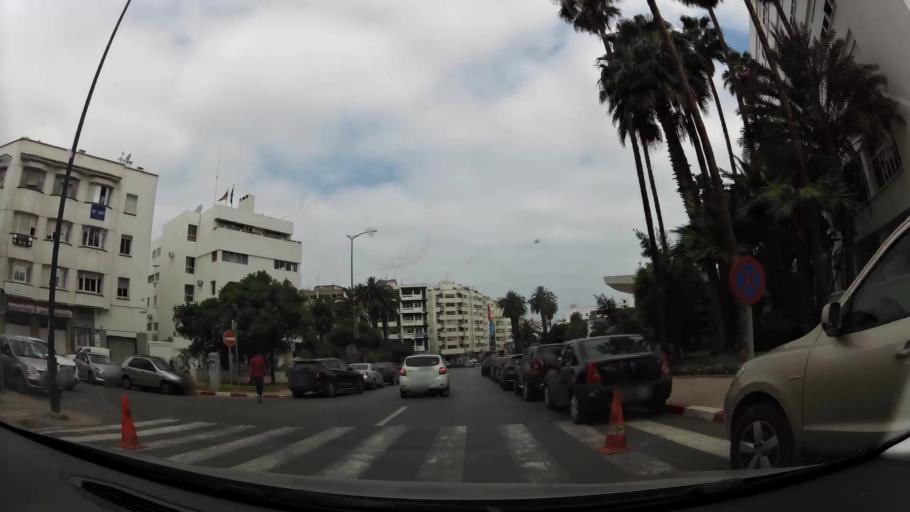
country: MA
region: Rabat-Sale-Zemmour-Zaer
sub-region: Rabat
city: Rabat
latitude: 34.0186
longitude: -6.8328
